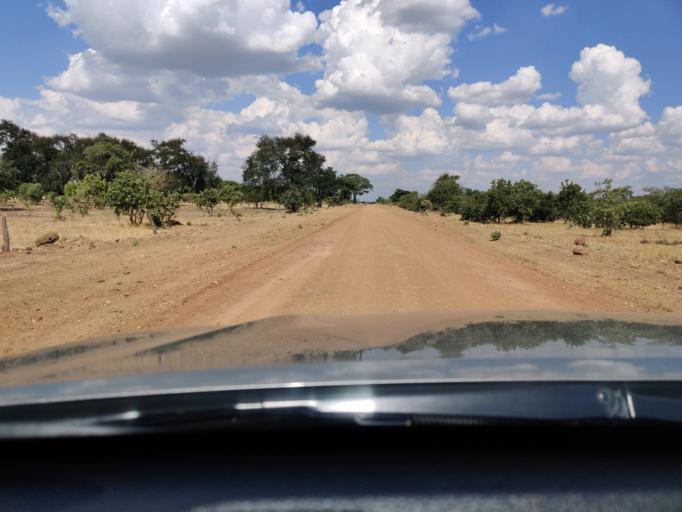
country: ZM
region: Central
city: Chibombo
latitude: -14.7592
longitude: 27.8698
